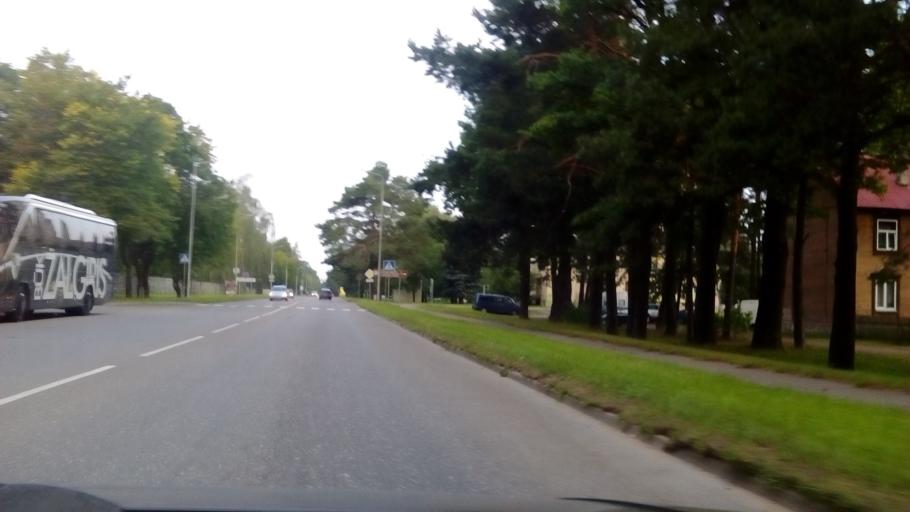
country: LT
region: Alytaus apskritis
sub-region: Alytus
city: Alytus
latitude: 54.3810
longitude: 24.0588
